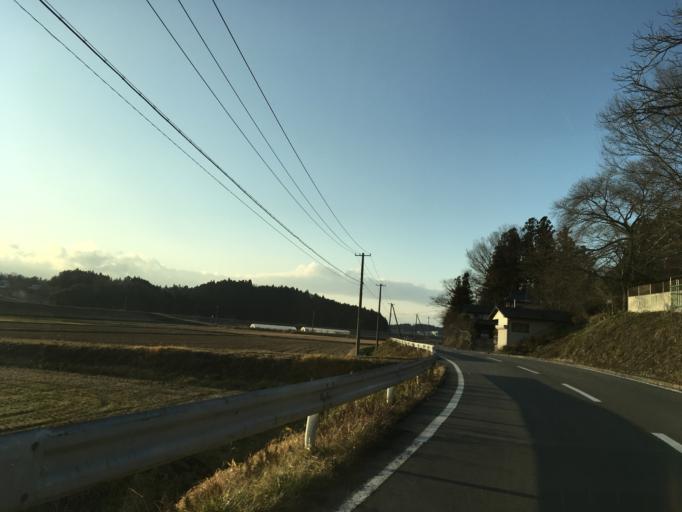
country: JP
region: Iwate
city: Ichinoseki
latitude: 38.8080
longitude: 141.2179
